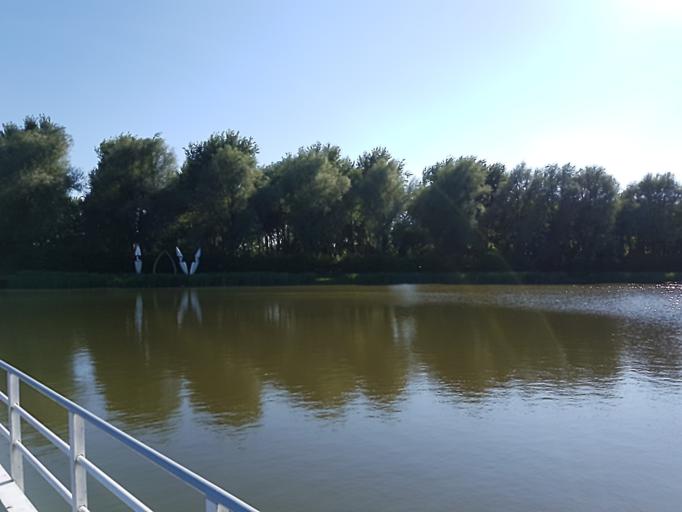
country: NL
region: South Holland
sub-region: Gemeente Pijnacker-Nootdorp
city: Pijnacker
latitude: 52.0413
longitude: 4.4586
